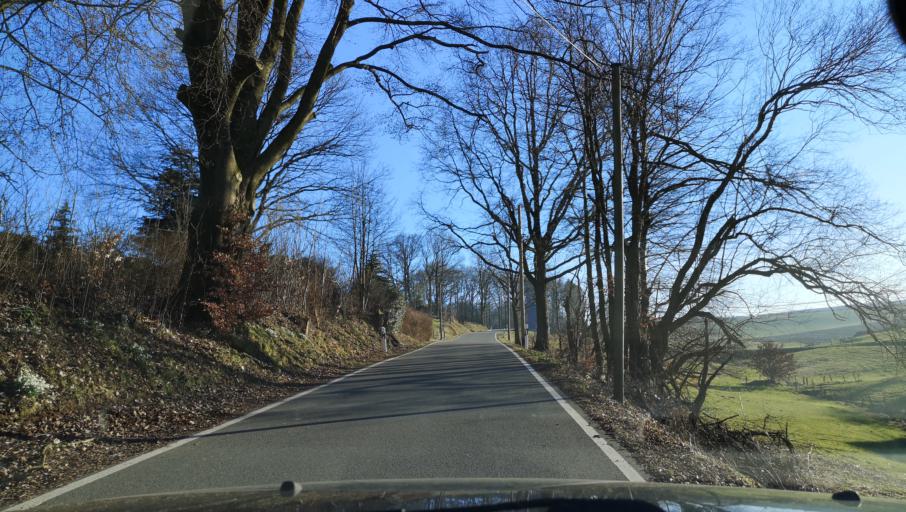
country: DE
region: North Rhine-Westphalia
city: Radevormwald
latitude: 51.2088
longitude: 7.4072
